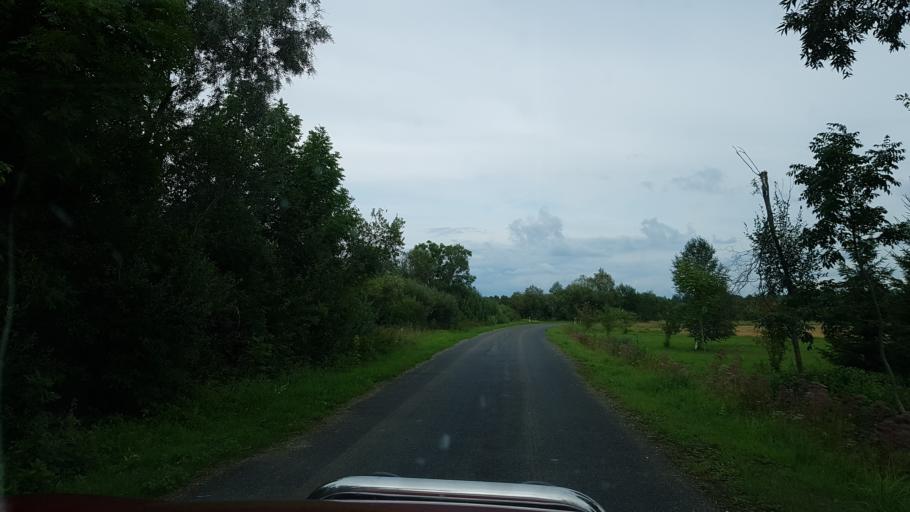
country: EE
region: Laeaene
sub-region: Ridala Parish
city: Uuemoisa
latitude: 58.9836
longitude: 23.8036
